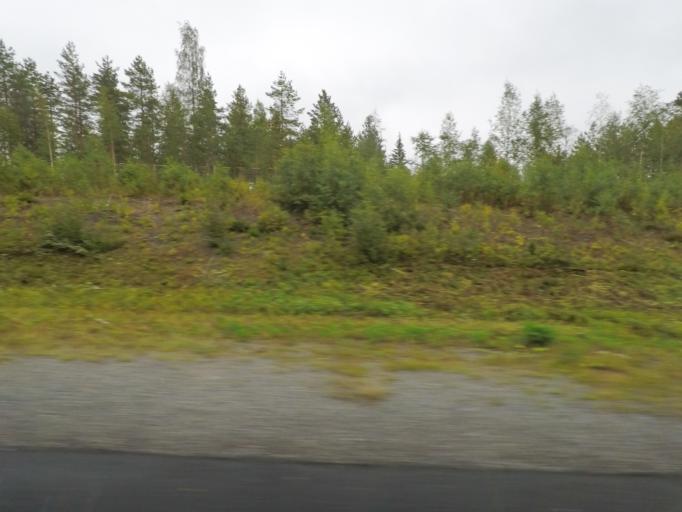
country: FI
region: Northern Savo
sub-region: Kuopio
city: Kuopio
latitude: 62.7606
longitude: 27.5807
